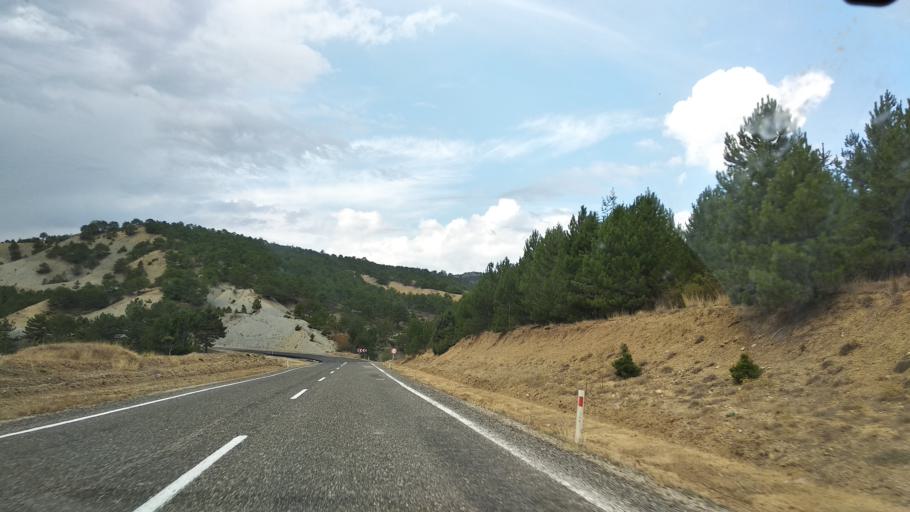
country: TR
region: Bolu
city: Seben
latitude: 40.3592
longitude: 31.4837
